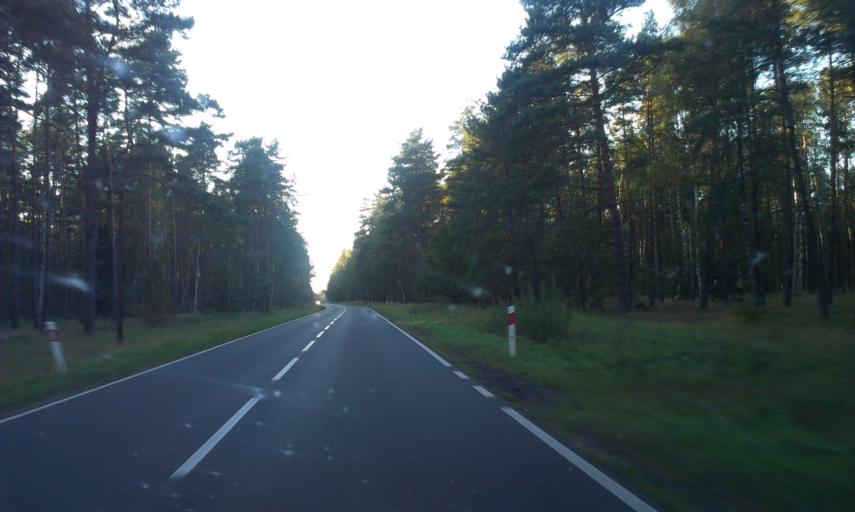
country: PL
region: Pomeranian Voivodeship
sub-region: Powiat czluchowski
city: Czarne
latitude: 53.7153
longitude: 16.8490
